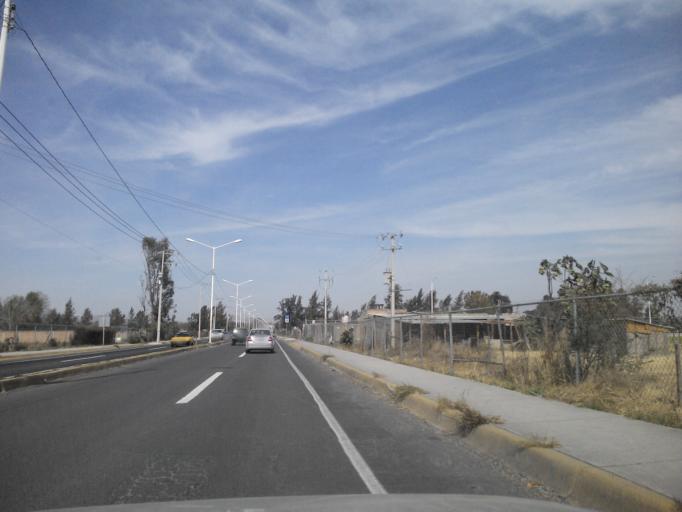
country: MX
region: Jalisco
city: San Sebastian el Grande
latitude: 20.5175
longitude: -103.4105
